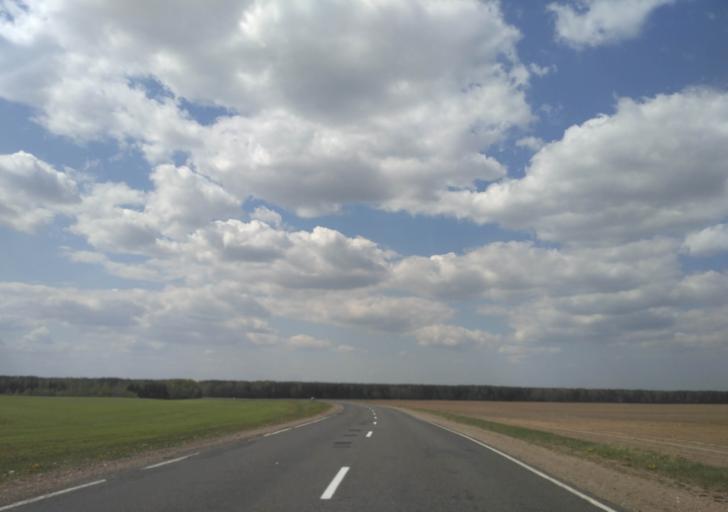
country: BY
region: Minsk
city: Vilyeyka
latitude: 54.5178
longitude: 27.0266
